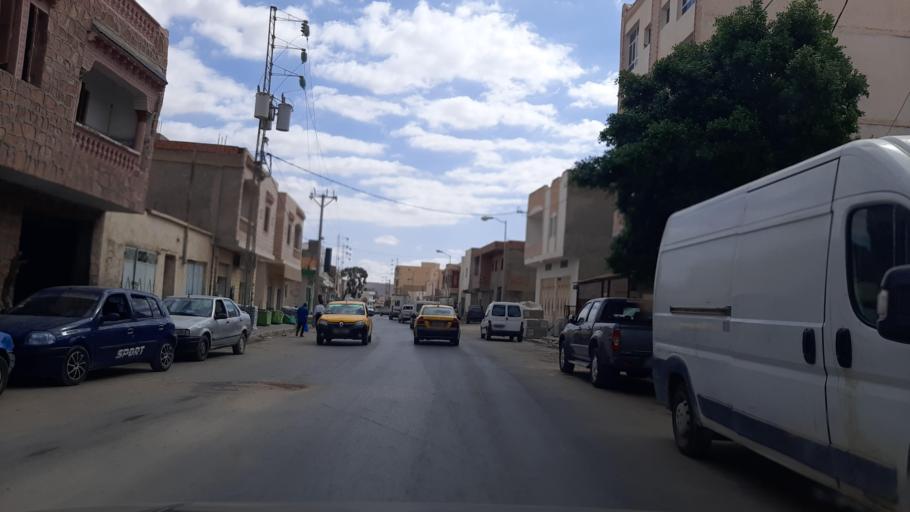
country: TN
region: Tataouine
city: Tataouine
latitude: 32.9260
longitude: 10.4520
